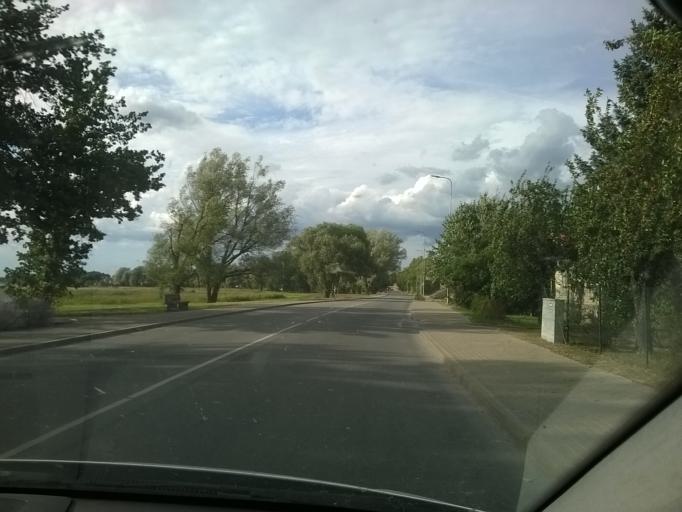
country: EE
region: Vorumaa
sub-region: Voru linn
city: Voru
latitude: 57.8360
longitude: 27.0037
